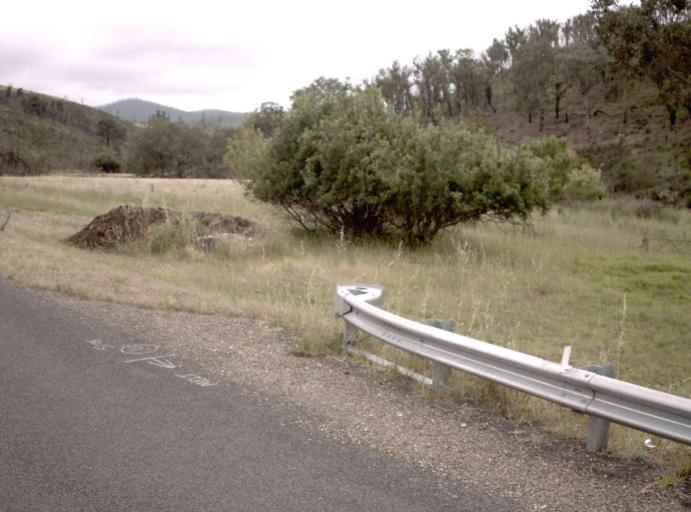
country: AU
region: Victoria
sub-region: Wellington
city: Heyfield
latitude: -37.8540
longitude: 146.7069
